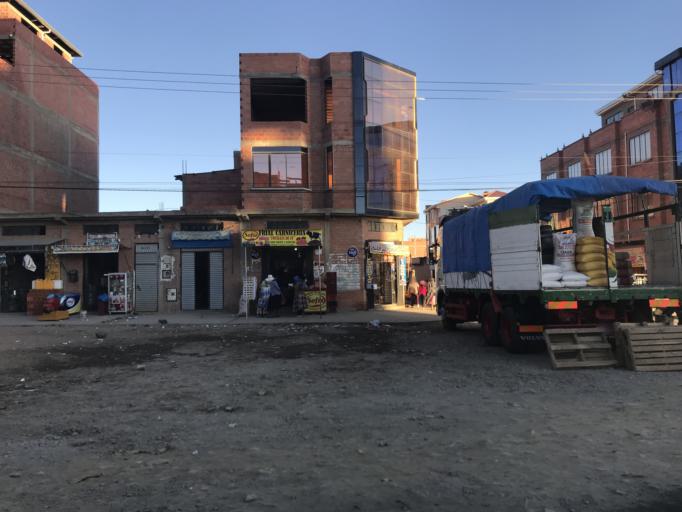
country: BO
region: La Paz
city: La Paz
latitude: -16.5039
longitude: -68.2481
